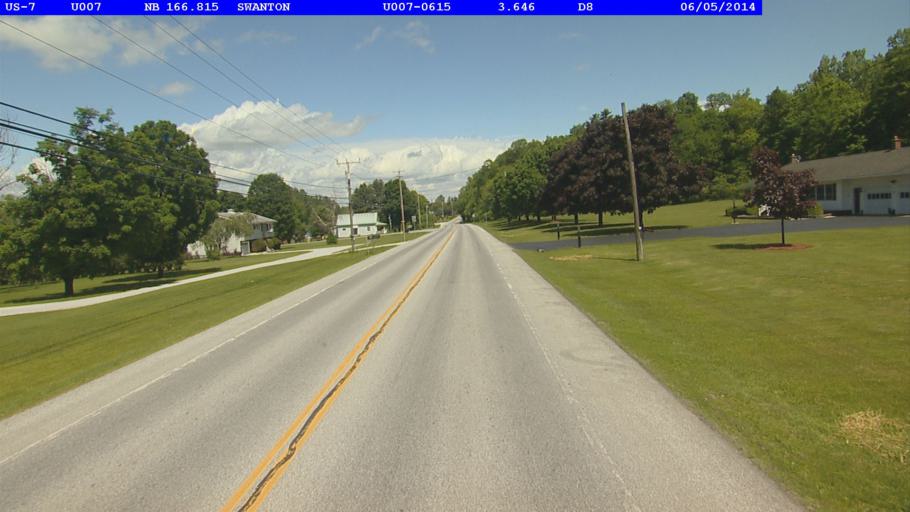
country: US
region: Vermont
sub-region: Franklin County
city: Swanton
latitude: 44.8981
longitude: -73.0947
